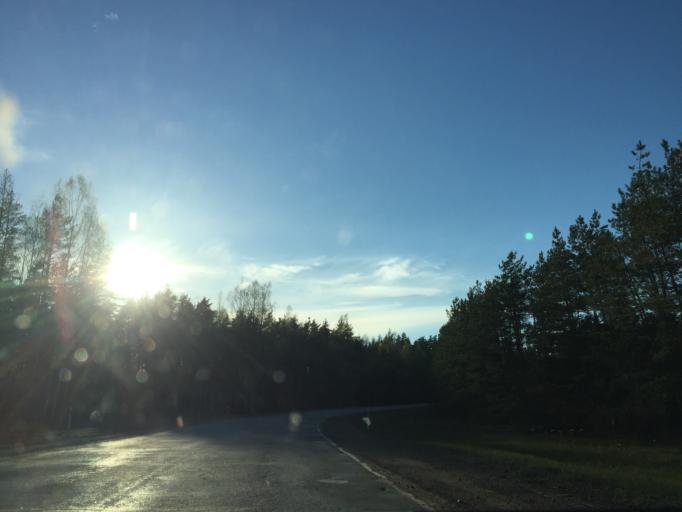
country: LV
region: Strenci
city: Seda
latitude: 57.6260
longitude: 25.7462
